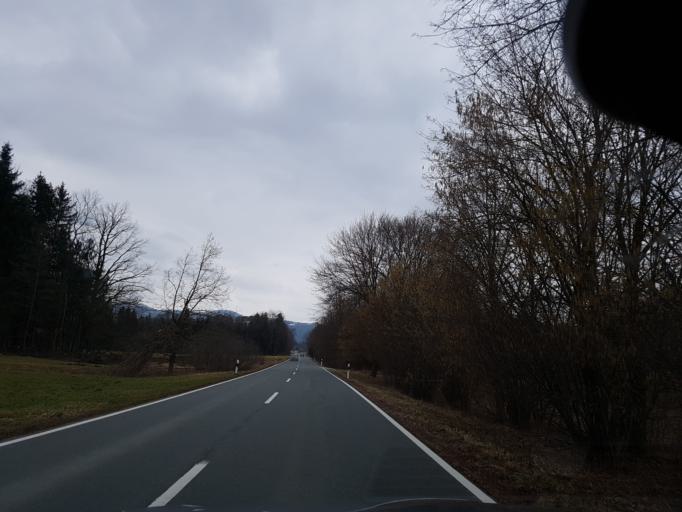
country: DE
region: Bavaria
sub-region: Upper Bavaria
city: Bad Aibling
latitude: 47.8328
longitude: 11.9801
